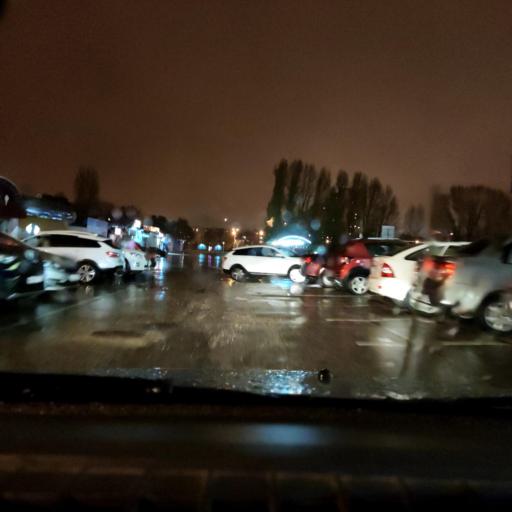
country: RU
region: Samara
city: Tol'yatti
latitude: 53.5184
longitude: 49.2710
